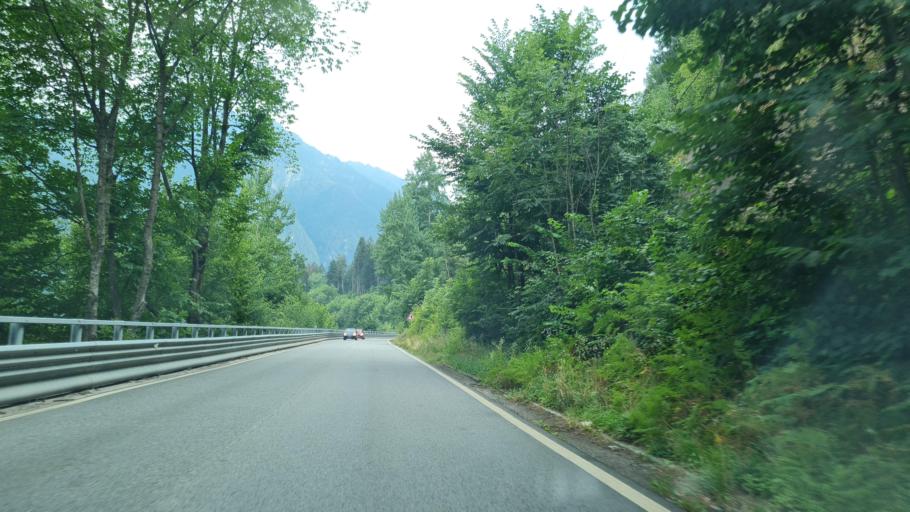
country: IT
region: Piedmont
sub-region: Provincia Verbano-Cusio-Ossola
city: Baceno
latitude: 46.2539
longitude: 8.3197
